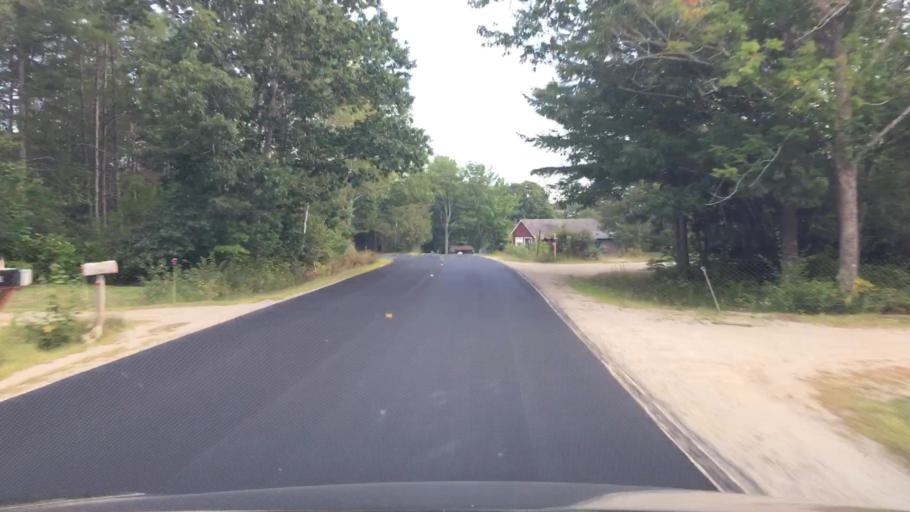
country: US
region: Maine
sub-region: Hancock County
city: Orland
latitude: 44.5465
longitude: -68.6203
